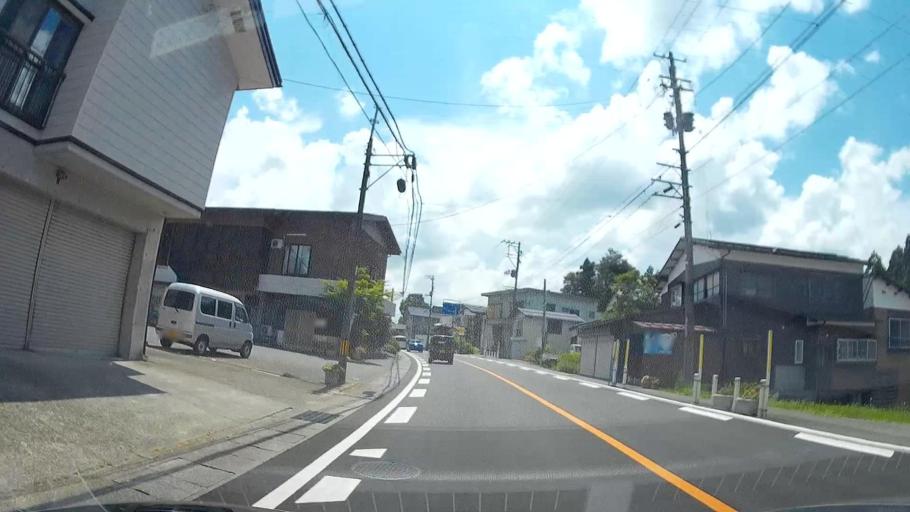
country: JP
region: Niigata
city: Tokamachi
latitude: 37.0767
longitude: 138.7170
